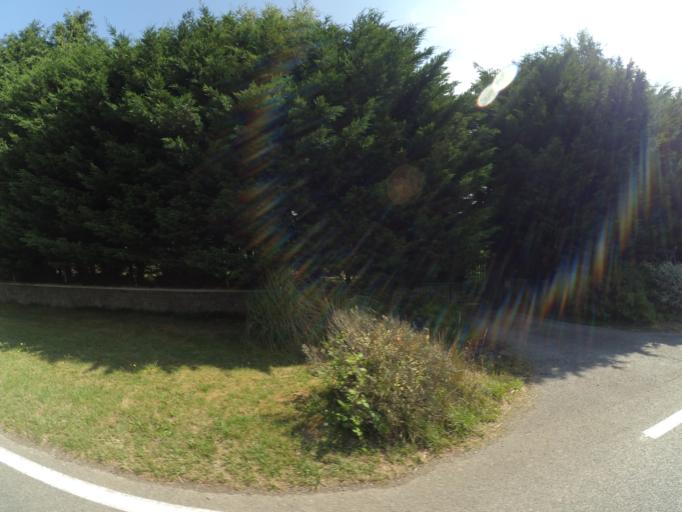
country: FR
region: Brittany
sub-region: Departement du Finistere
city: Mellac
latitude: 47.8915
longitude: -3.5654
